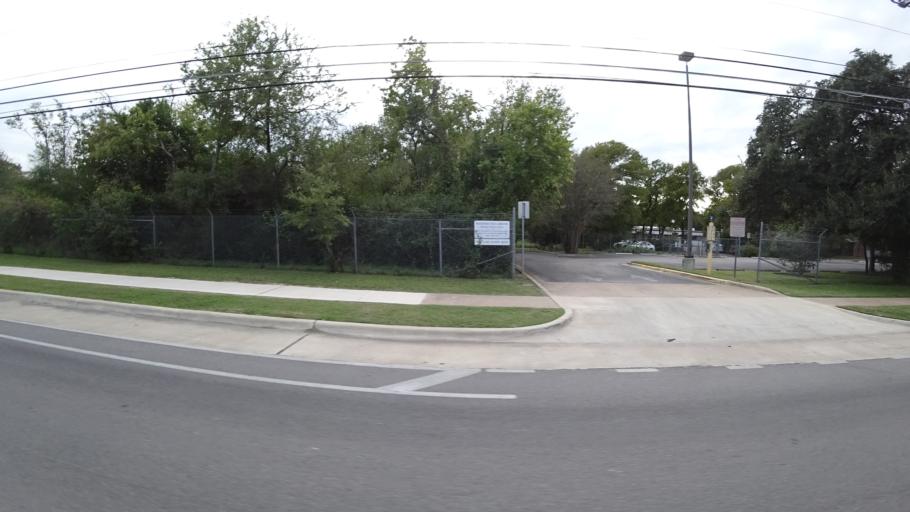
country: US
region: Texas
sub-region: Travis County
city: Rollingwood
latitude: 30.2839
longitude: -97.7774
